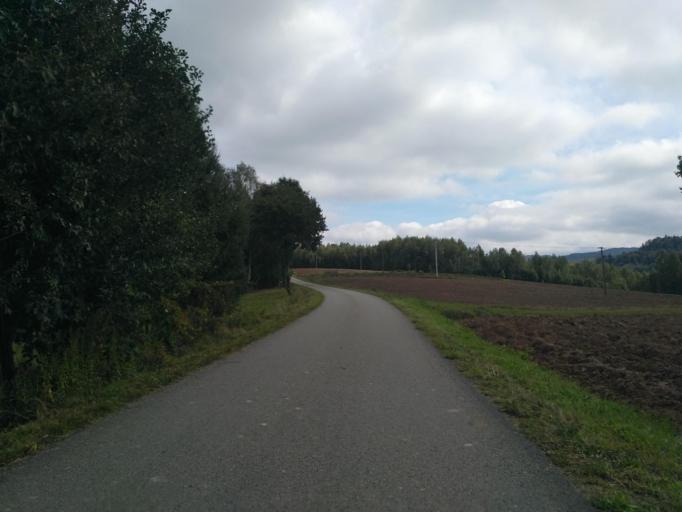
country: PL
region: Subcarpathian Voivodeship
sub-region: Powiat ropczycko-sedziszowski
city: Niedzwiada
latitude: 49.9204
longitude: 21.4878
